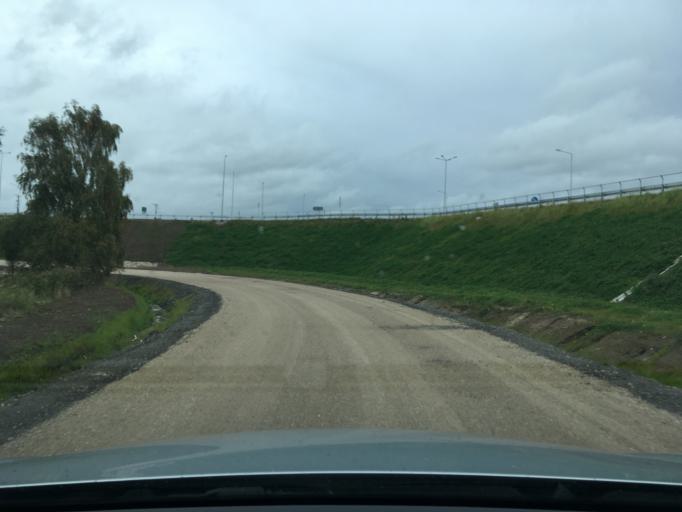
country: PL
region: Pomeranian Voivodeship
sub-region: Powiat koscierski
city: Koscierzyna
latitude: 54.1059
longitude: 17.9754
